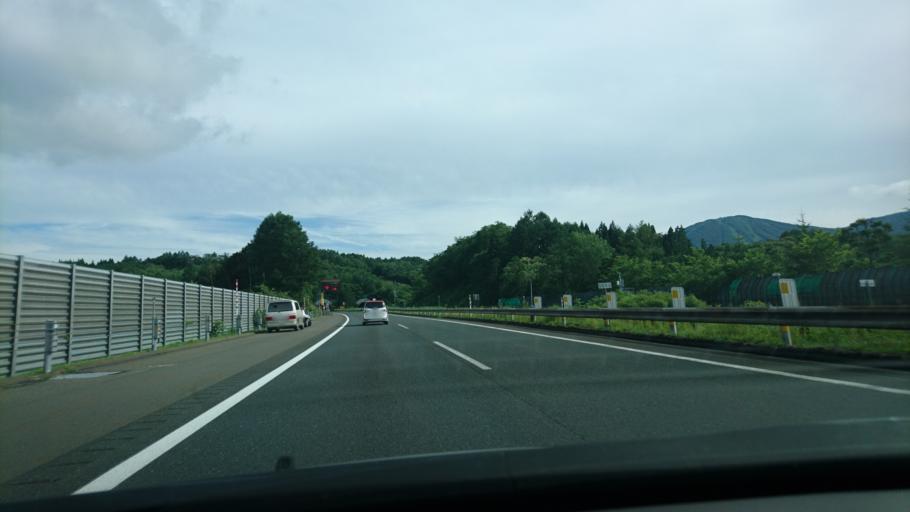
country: JP
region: Akita
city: Hanawa
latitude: 40.0239
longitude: 140.9832
